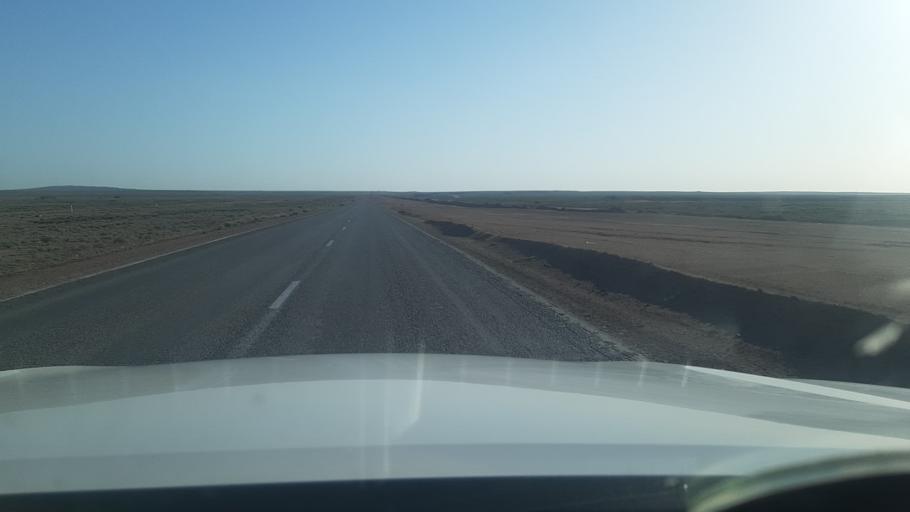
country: KZ
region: Qaraghandy
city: Saryshaghan
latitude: 46.4842
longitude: 74.0583
